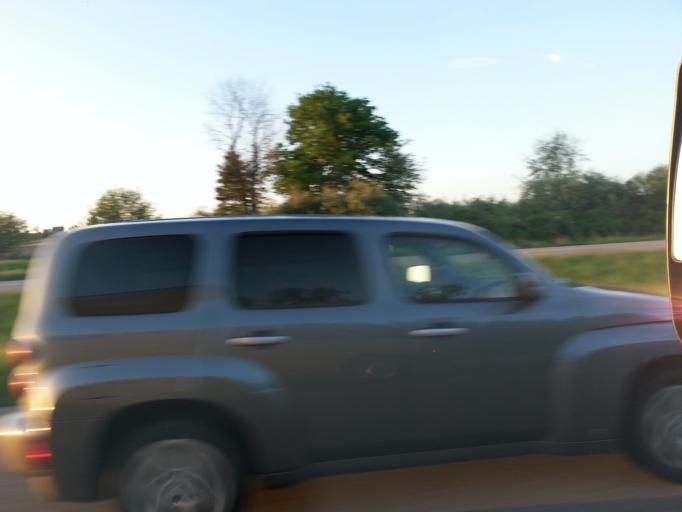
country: US
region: Indiana
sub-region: Fountain County
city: Veedersburg
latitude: 40.1086
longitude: -87.0866
